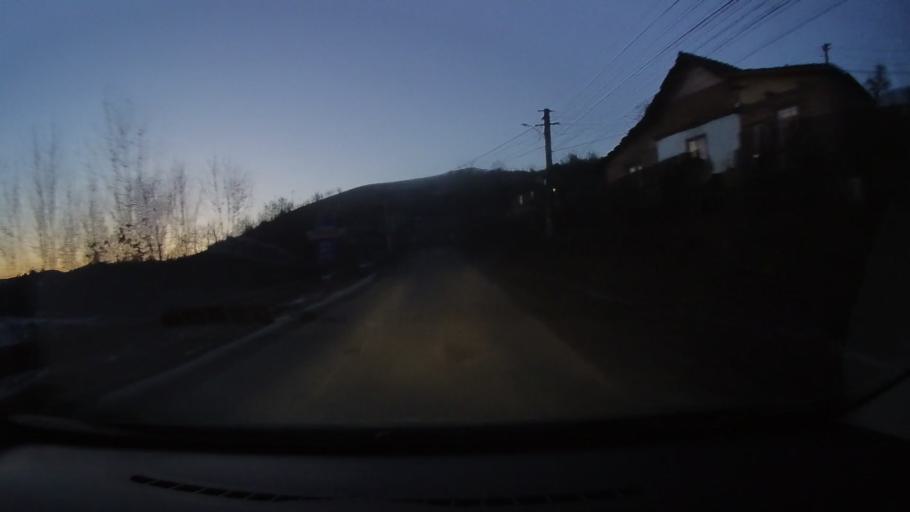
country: RO
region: Sibiu
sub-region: Comuna Darlos
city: Darlos
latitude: 46.1875
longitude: 24.3944
